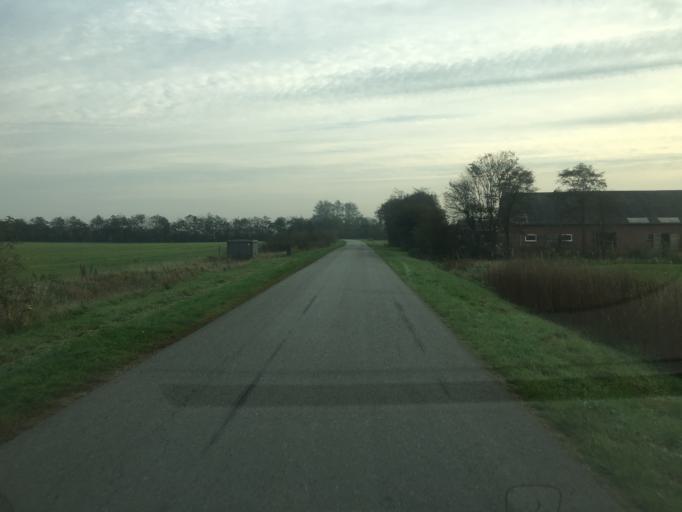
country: DK
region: South Denmark
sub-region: Tonder Kommune
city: Toftlund
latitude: 55.1017
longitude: 9.0392
